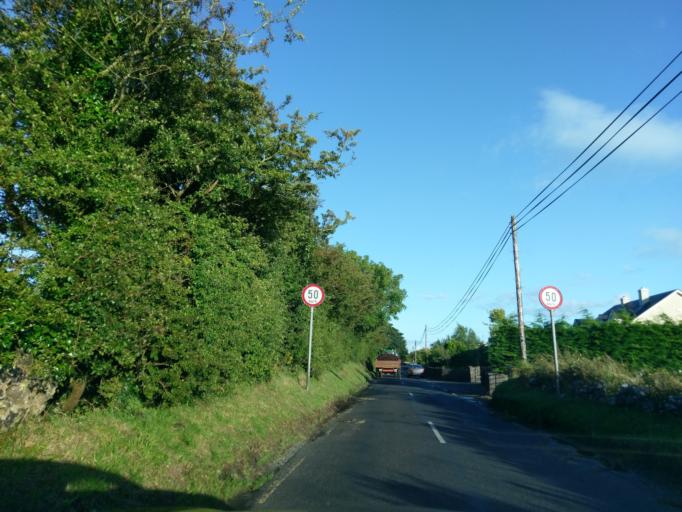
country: IE
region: Connaught
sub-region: County Galway
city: Athenry
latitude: 53.3787
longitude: -8.7136
